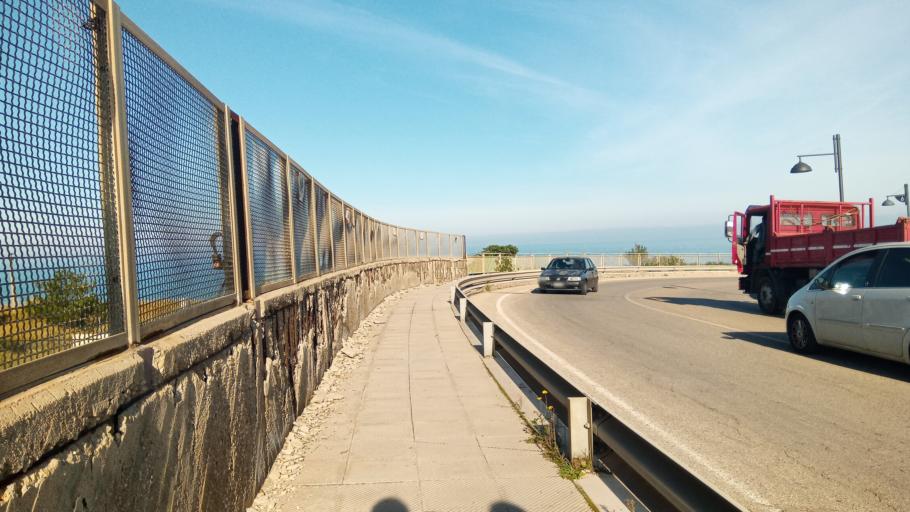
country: IT
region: Molise
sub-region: Provincia di Campobasso
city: Termoli
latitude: 42.0039
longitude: 14.9885
